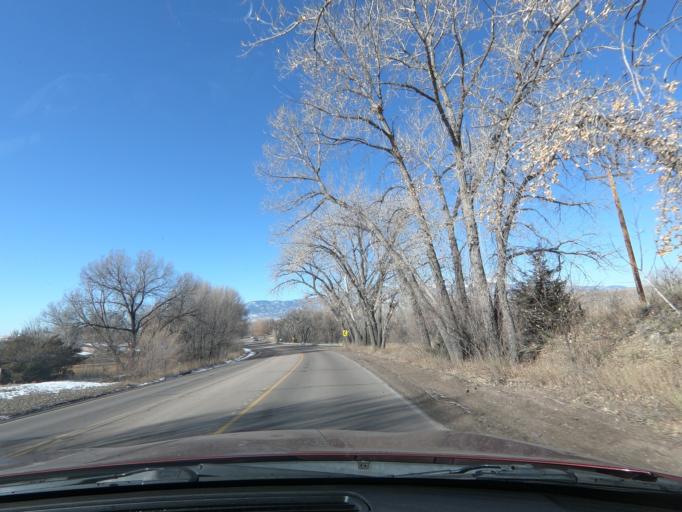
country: US
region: Colorado
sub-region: El Paso County
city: Security-Widefield
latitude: 38.7375
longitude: -104.7074
